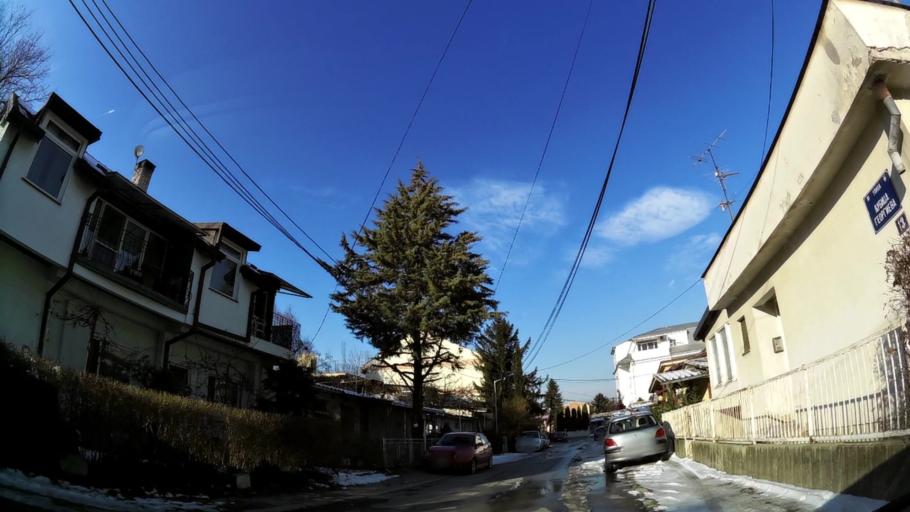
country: MK
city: Krushopek
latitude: 41.9993
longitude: 21.3880
